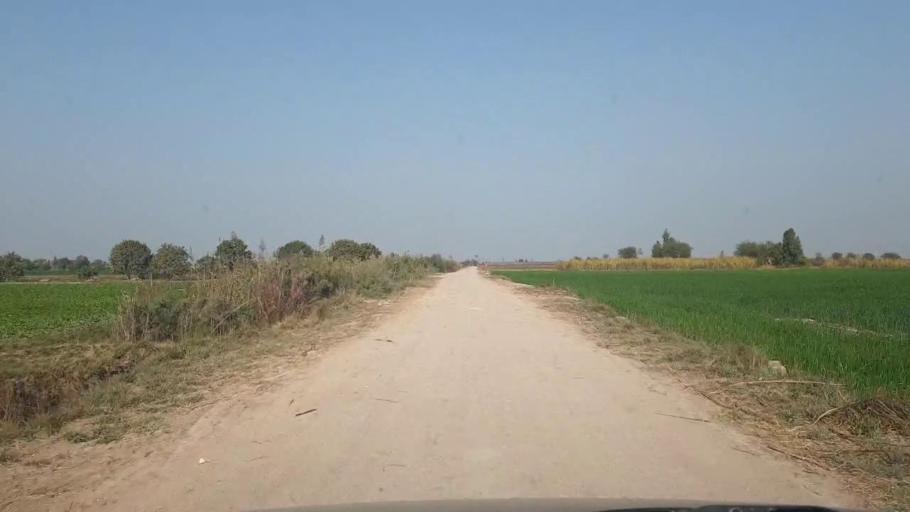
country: PK
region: Sindh
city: Bhit Shah
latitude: 25.8193
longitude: 68.5726
